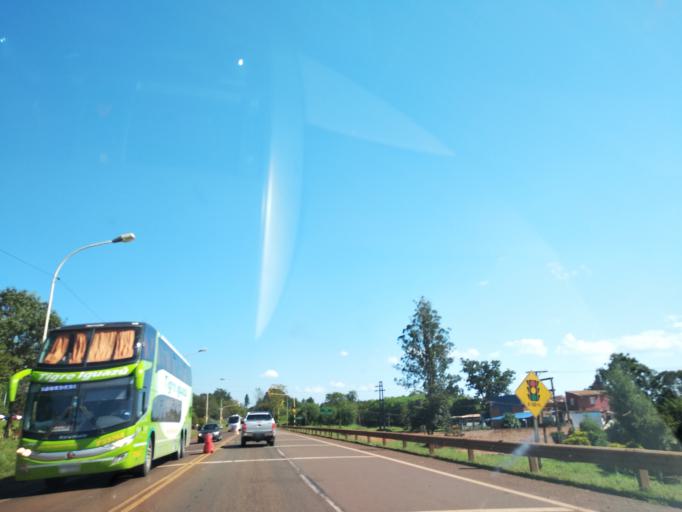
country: AR
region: Misiones
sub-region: Departamento de Eldorado
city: Eldorado
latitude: -26.4141
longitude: -54.6413
